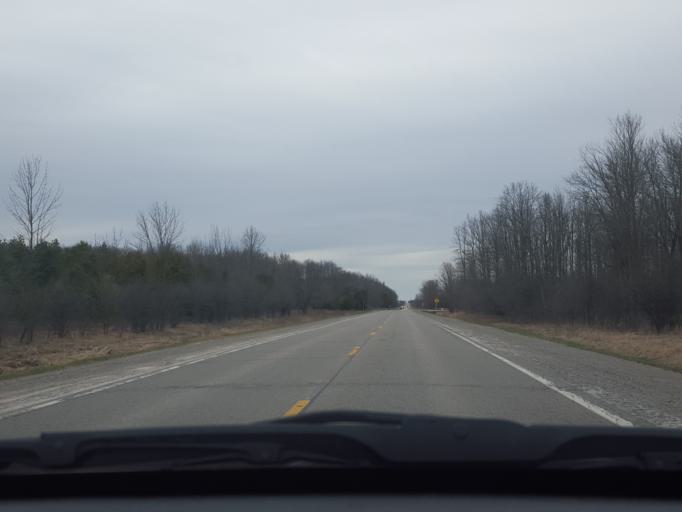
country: CA
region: Ontario
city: Uxbridge
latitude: 44.2921
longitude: -79.1689
